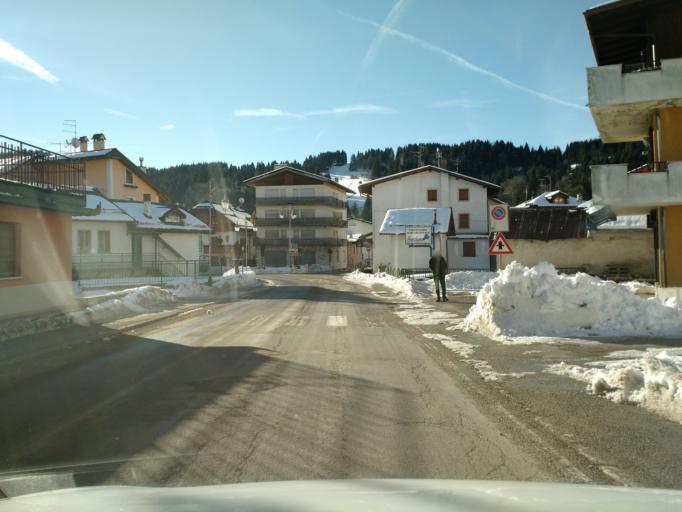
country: IT
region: Veneto
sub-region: Provincia di Vicenza
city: Canove di Roana
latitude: 45.8391
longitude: 11.4534
